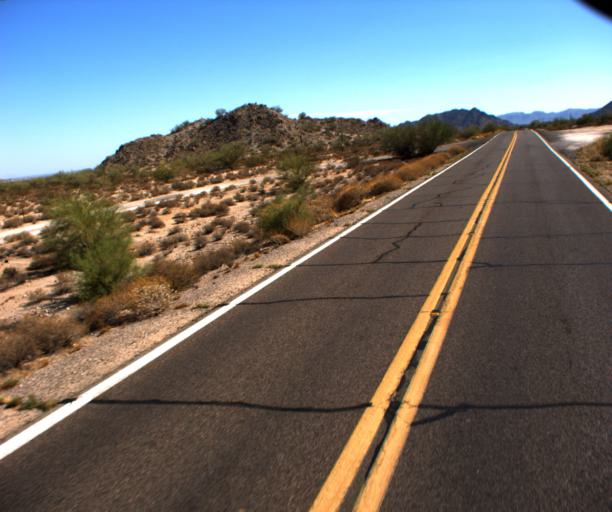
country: US
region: Arizona
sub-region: Pinal County
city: Sacaton
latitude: 33.0077
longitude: -111.7501
